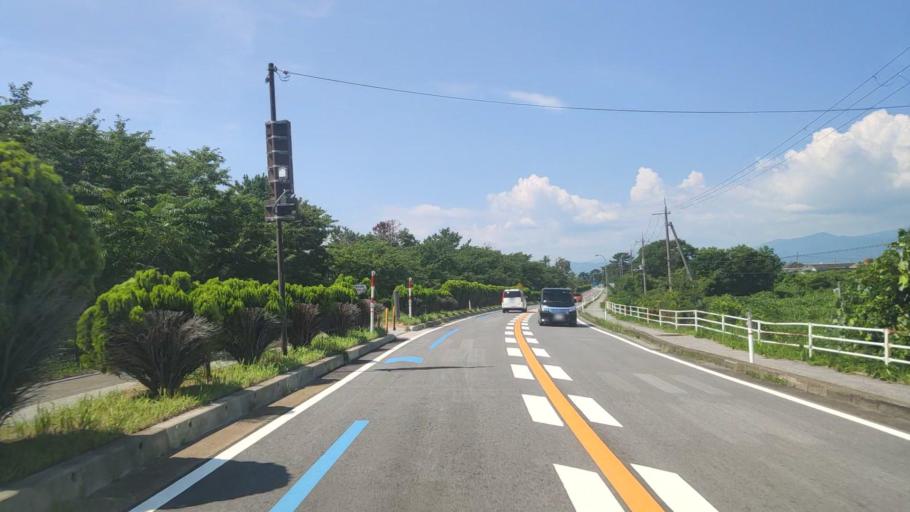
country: JP
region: Shiga Prefecture
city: Nagahama
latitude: 35.3918
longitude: 136.2174
